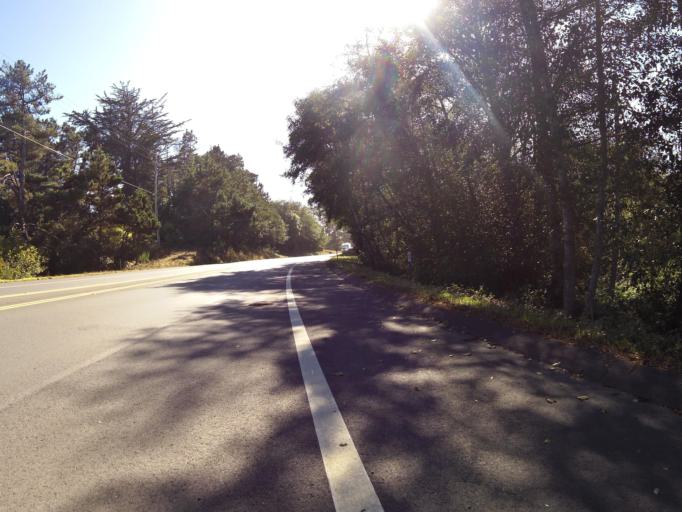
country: US
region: California
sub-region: Mendocino County
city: Fort Bragg
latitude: 39.4867
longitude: -123.7883
